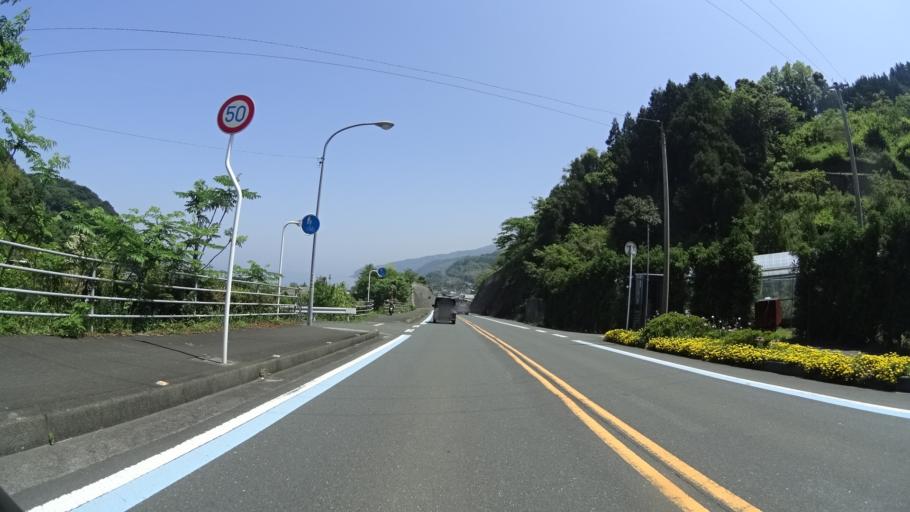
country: JP
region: Ehime
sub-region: Nishiuwa-gun
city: Ikata-cho
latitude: 33.5396
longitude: 132.4136
